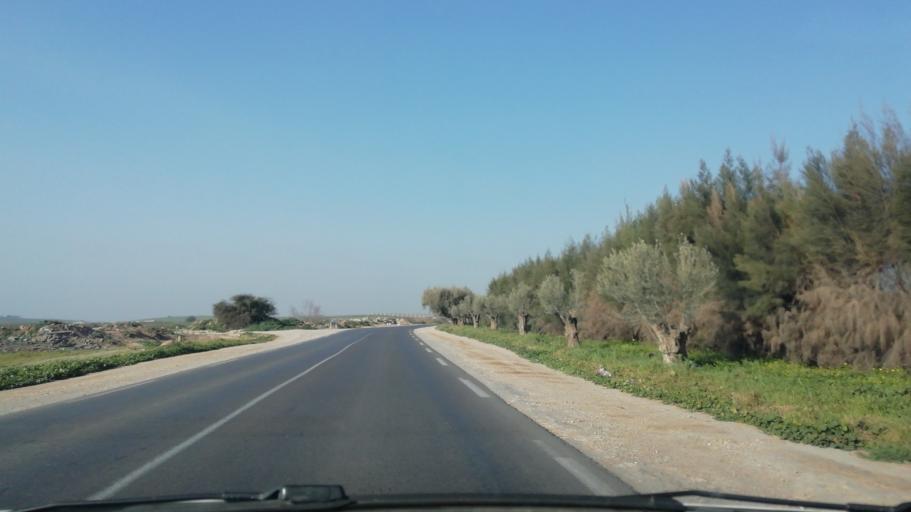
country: DZ
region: Mostaganem
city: Mostaganem
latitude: 35.7450
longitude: 0.1502
